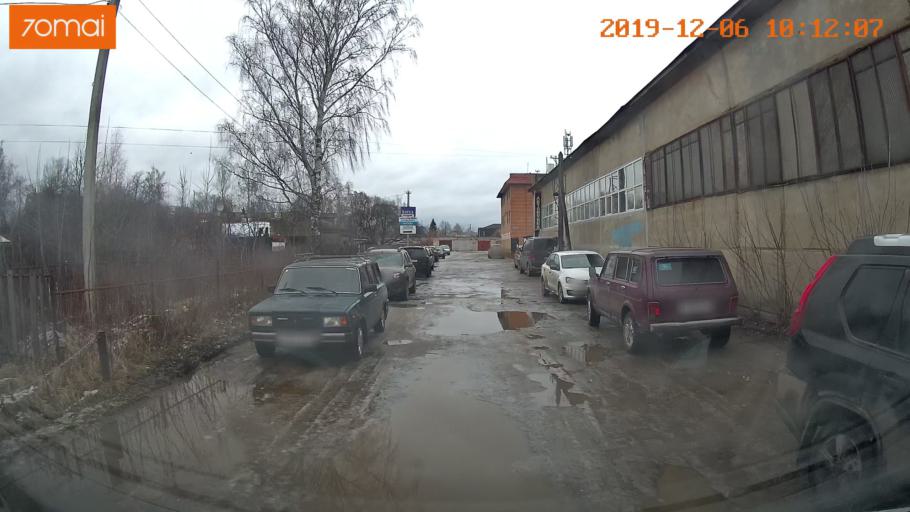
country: RU
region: Ivanovo
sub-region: Gorod Ivanovo
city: Ivanovo
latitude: 57.0321
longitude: 40.9743
